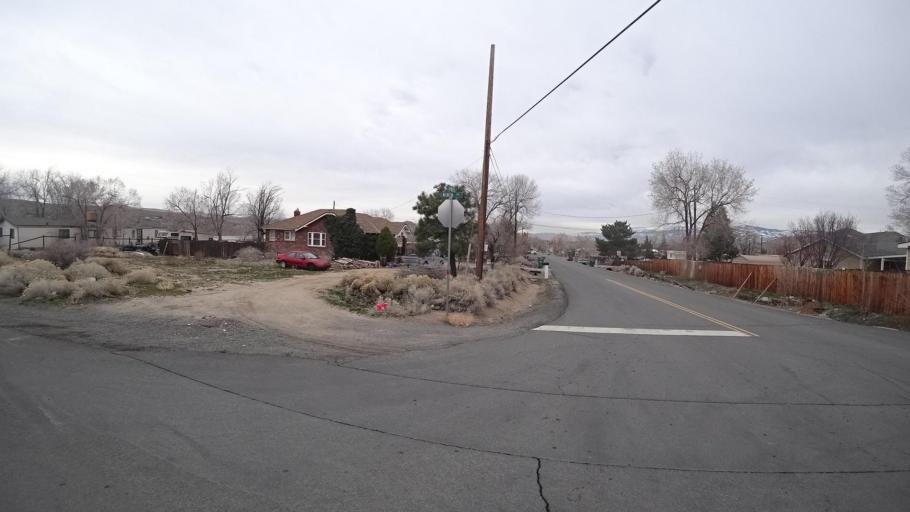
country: US
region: Nevada
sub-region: Washoe County
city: Sun Valley
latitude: 39.6072
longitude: -119.7710
